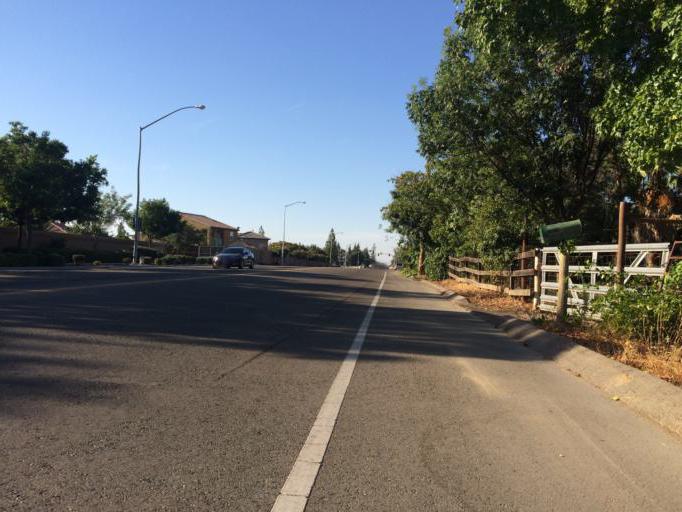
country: US
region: California
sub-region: Fresno County
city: Tarpey Village
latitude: 36.7916
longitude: -119.6731
